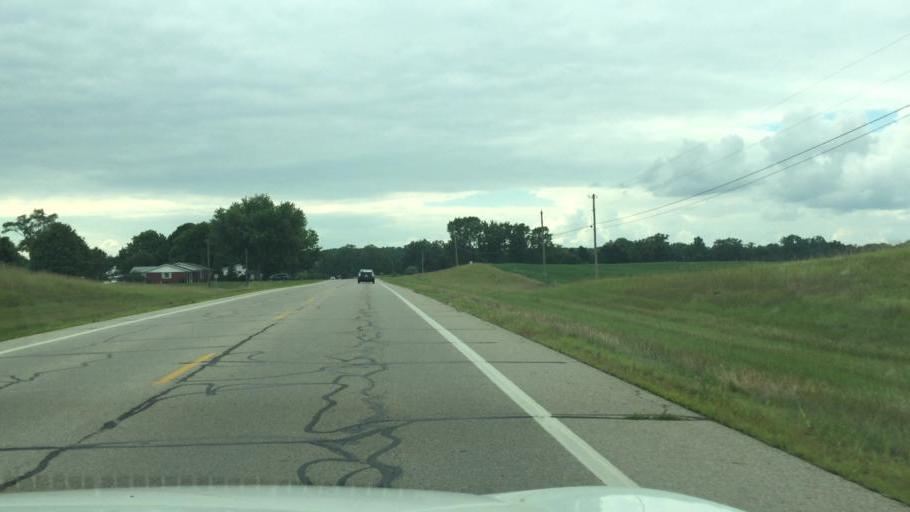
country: US
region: Ohio
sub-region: Champaign County
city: Mechanicsburg
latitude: 40.0768
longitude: -83.5736
